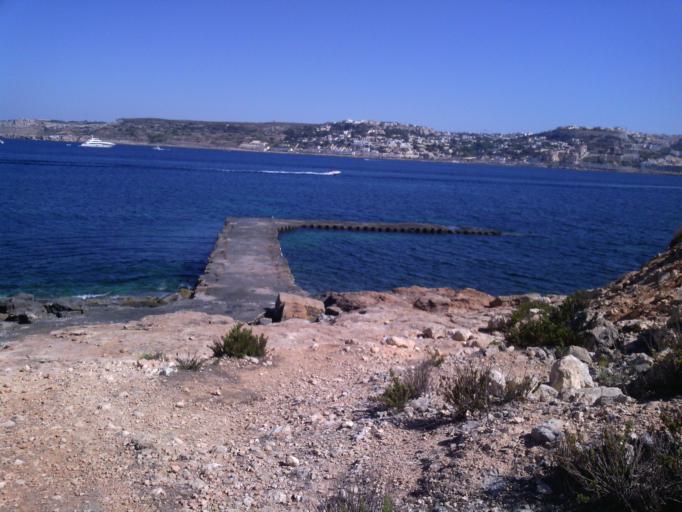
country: MT
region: Il-Mellieha
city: Mellieha
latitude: 35.9803
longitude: 14.3608
